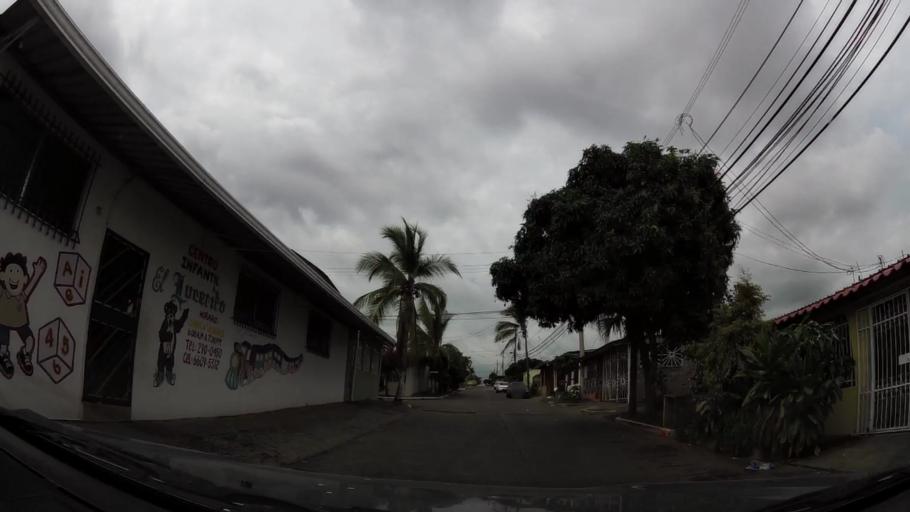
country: PA
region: Panama
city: San Miguelito
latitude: 9.0543
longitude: -79.4209
